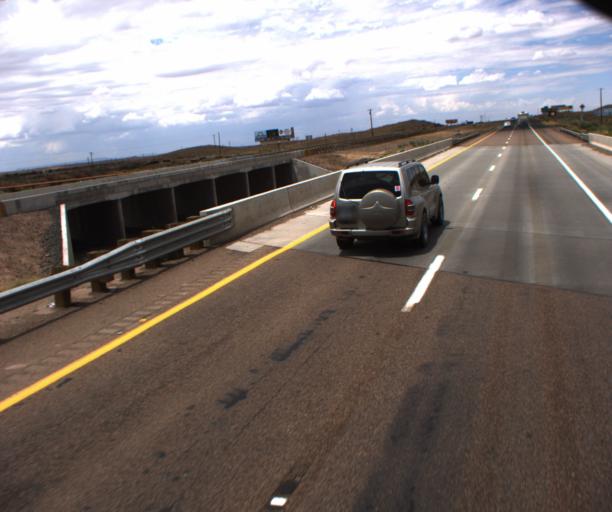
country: US
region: Arizona
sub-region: Navajo County
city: Joseph City
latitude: 34.9462
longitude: -110.2949
